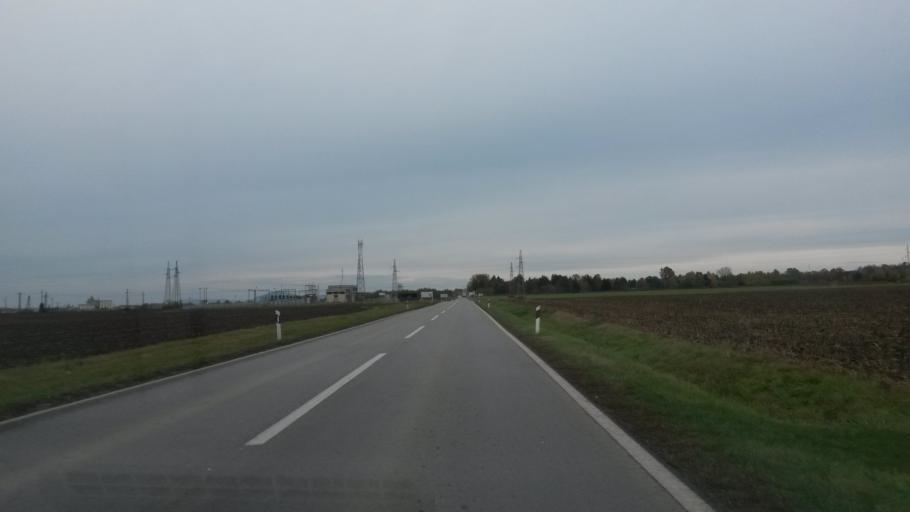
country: HR
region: Osjecko-Baranjska
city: Beli Manastir
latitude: 45.7566
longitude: 18.6322
